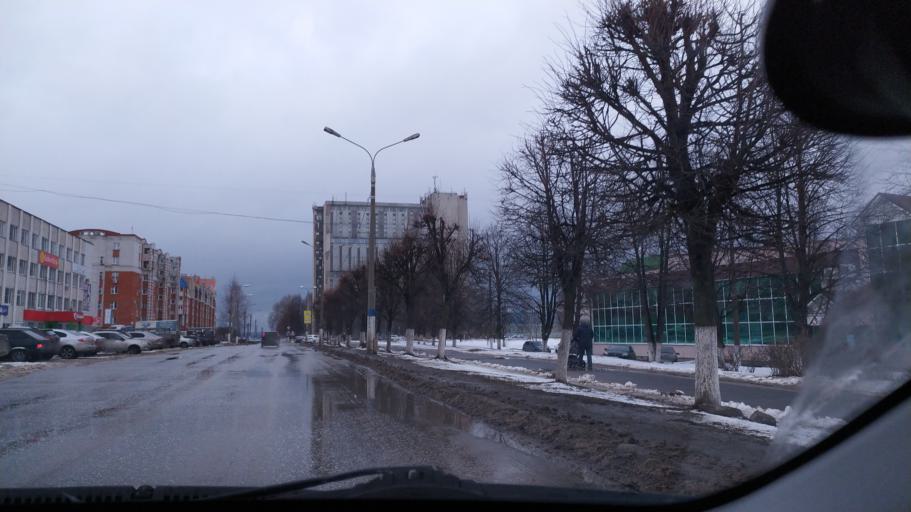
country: RU
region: Chuvashia
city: Novocheboksarsk
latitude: 56.1236
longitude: 47.4926
